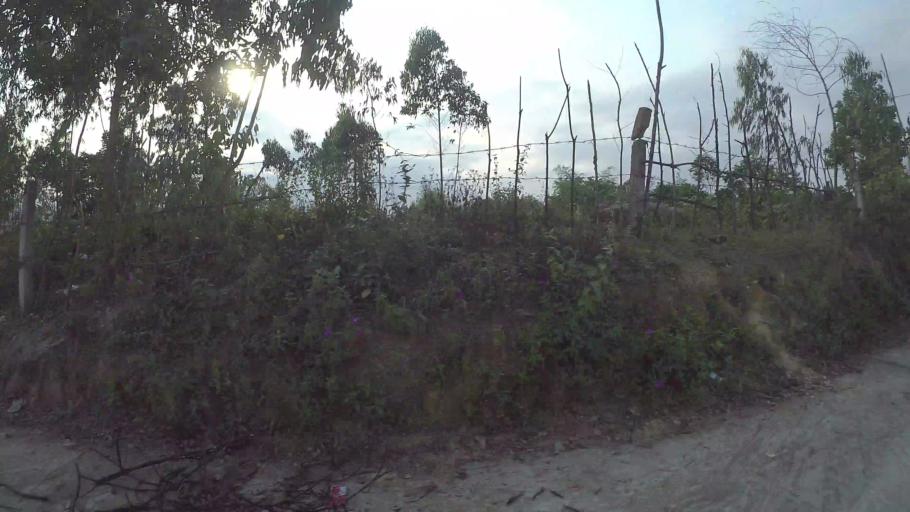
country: VN
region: Da Nang
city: Lien Chieu
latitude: 16.0541
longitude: 108.1073
